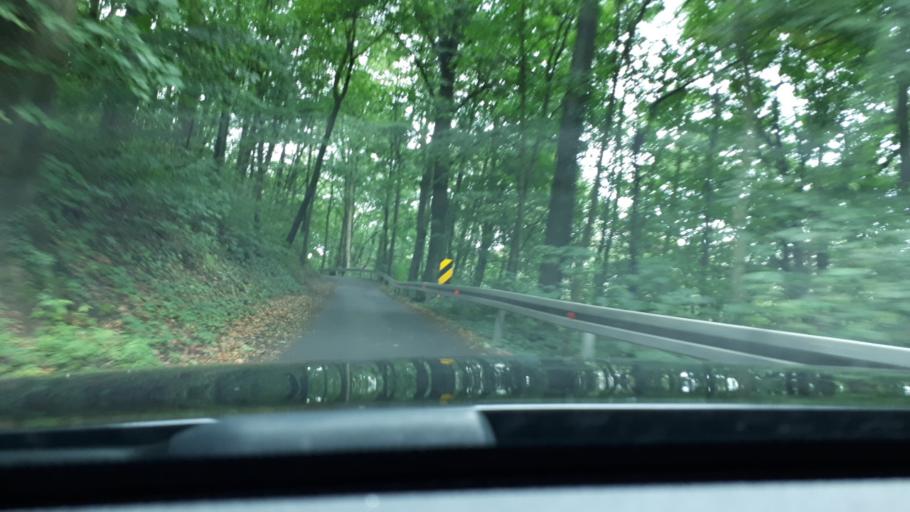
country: PL
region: Lower Silesian Voivodeship
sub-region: Powiat zlotoryjski
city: Olszanica
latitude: 51.1782
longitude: 15.7603
